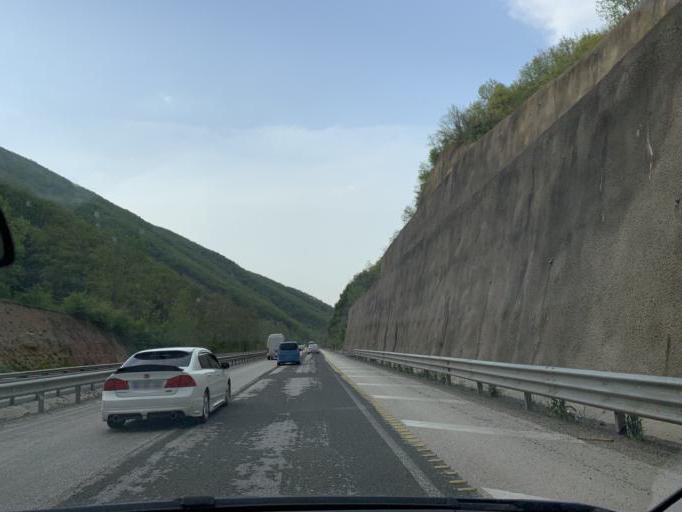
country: TR
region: Bursa
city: Kursunlu
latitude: 39.9984
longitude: 29.6535
